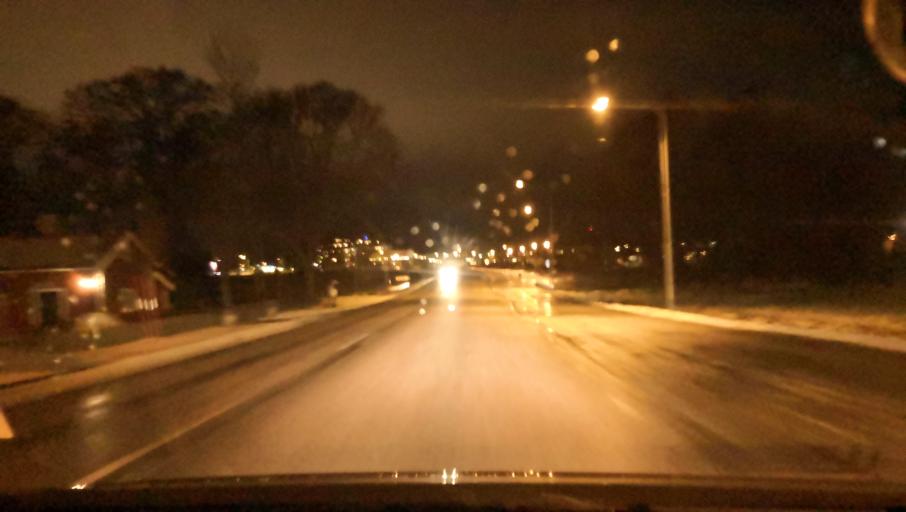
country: SE
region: Vaestmanland
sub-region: Vasteras
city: Tillberga
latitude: 59.5988
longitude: 16.7045
